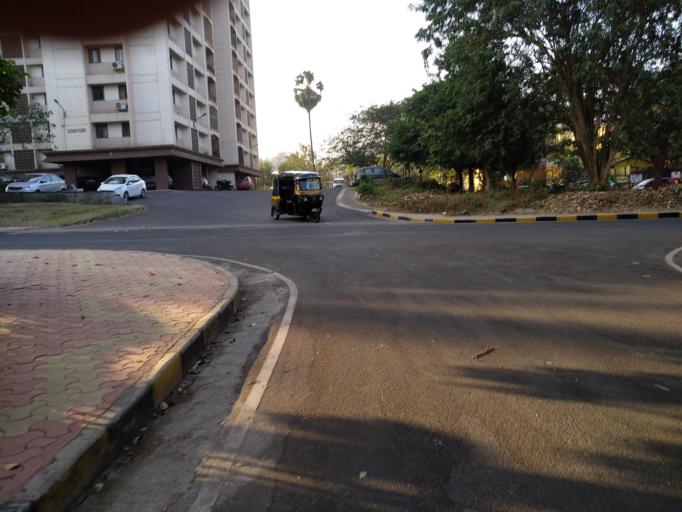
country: IN
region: Maharashtra
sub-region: Mumbai Suburban
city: Mumbai
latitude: 19.0355
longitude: 72.9287
